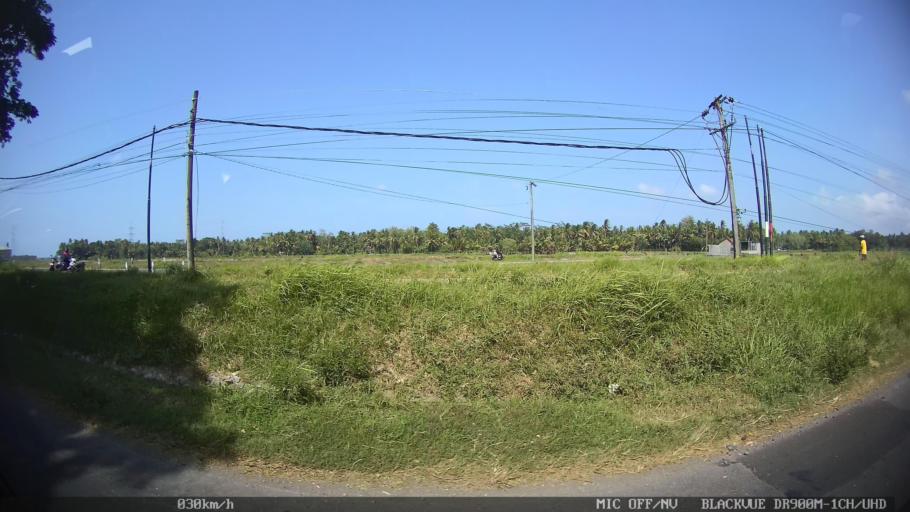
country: ID
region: Daerah Istimewa Yogyakarta
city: Srandakan
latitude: -7.9113
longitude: 110.1760
